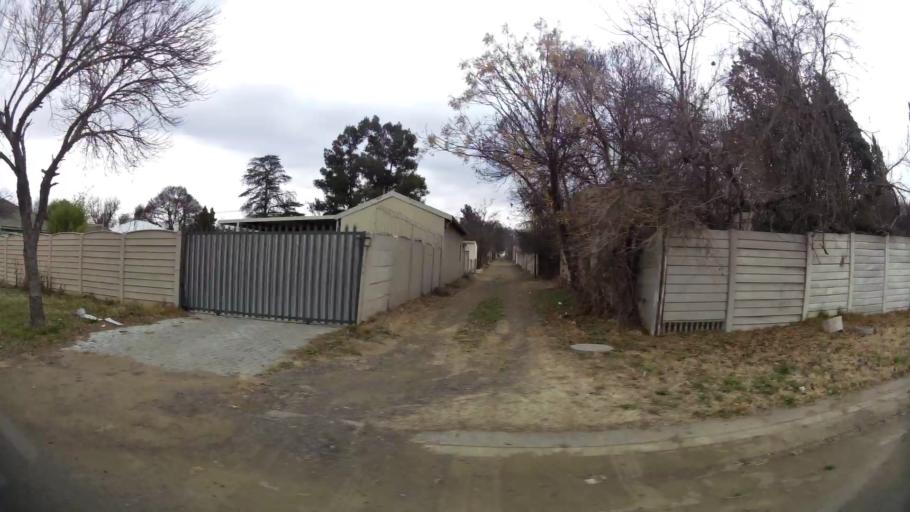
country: ZA
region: Orange Free State
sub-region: Fezile Dabi District Municipality
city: Kroonstad
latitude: -27.6553
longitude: 27.2455
